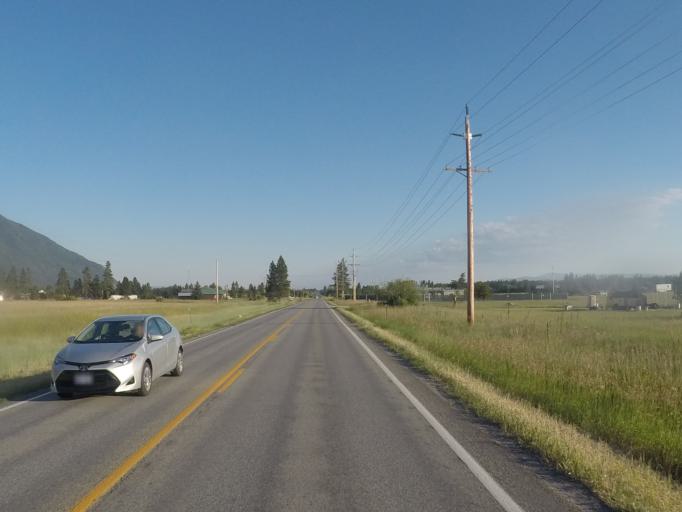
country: US
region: Montana
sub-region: Flathead County
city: Columbia Falls
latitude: 48.3525
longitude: -114.1593
